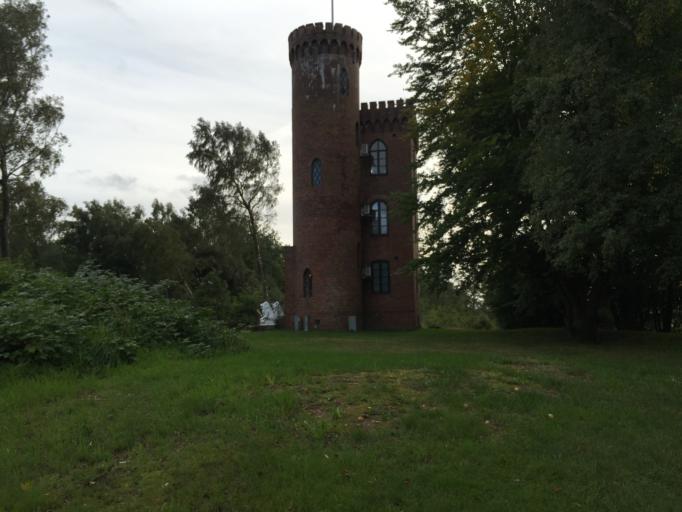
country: SE
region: Halland
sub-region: Laholms Kommun
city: Veinge
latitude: 56.5505
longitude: 13.0679
